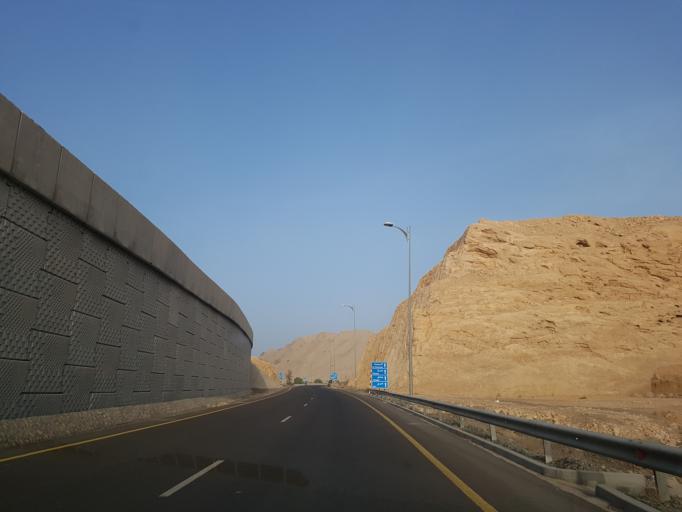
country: OM
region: Al Buraimi
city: Al Buraymi
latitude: 24.2311
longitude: 55.9529
